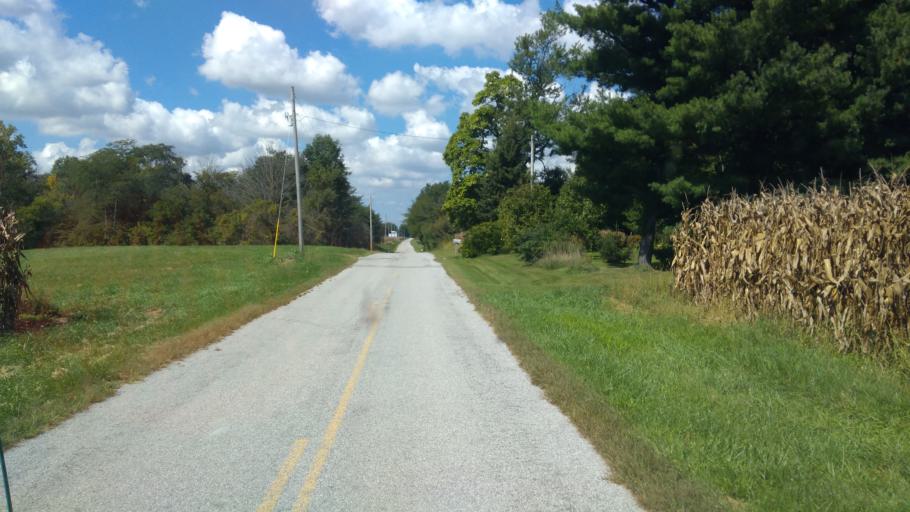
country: US
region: Ohio
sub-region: Wyandot County
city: Upper Sandusky
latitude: 40.6743
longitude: -83.3563
